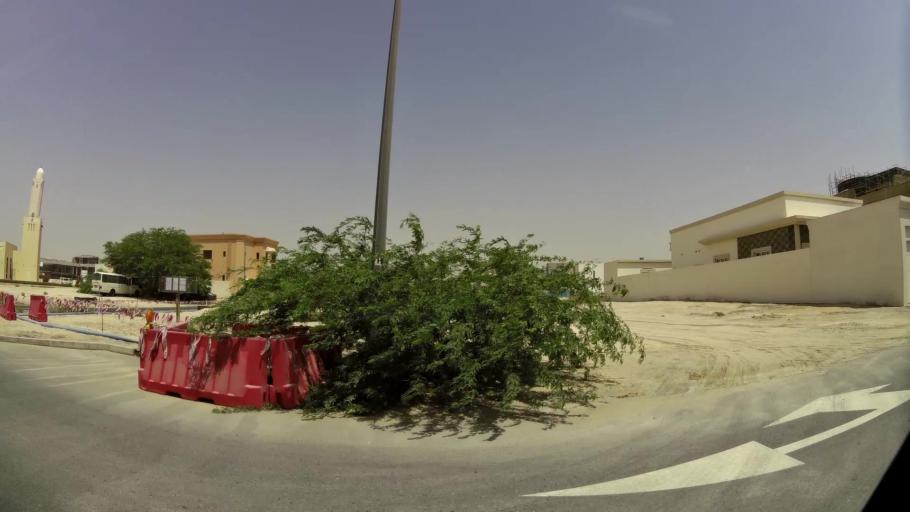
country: AE
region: Dubai
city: Dubai
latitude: 25.1361
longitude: 55.2028
